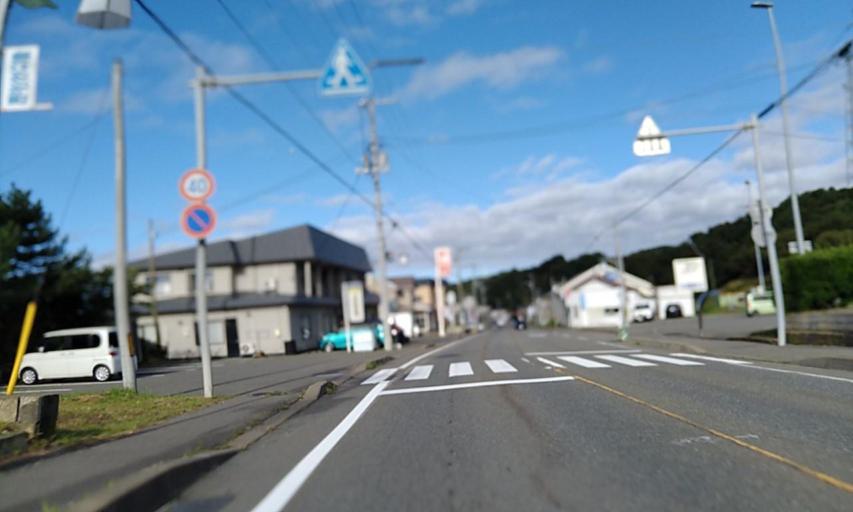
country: JP
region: Hokkaido
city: Shizunai-furukawacho
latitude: 42.2469
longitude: 142.5668
